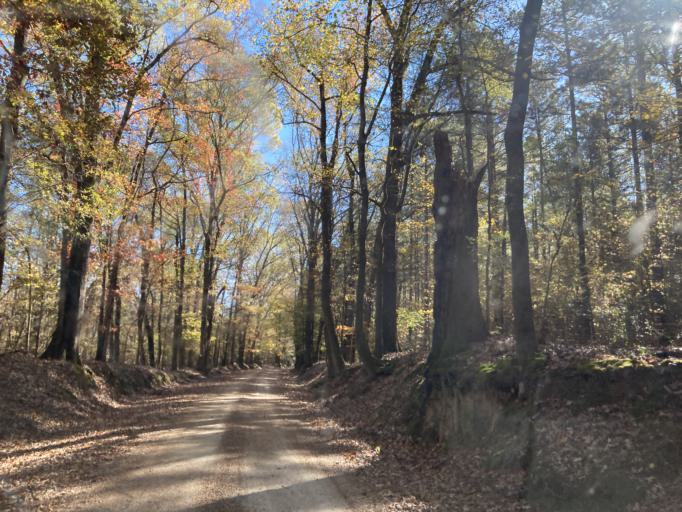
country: US
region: Mississippi
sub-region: Hinds County
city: Lynchburg
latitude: 32.5528
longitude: -90.4990
